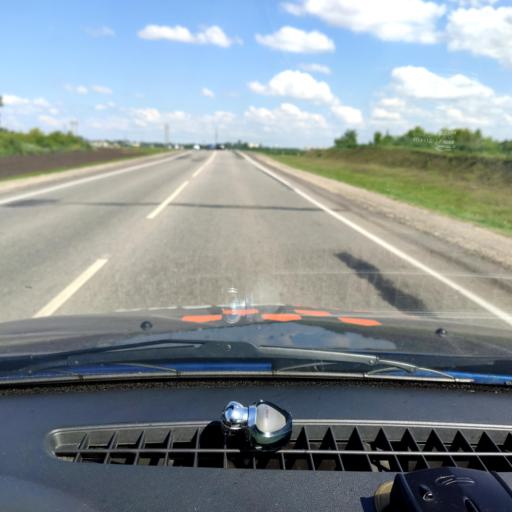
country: RU
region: Orjol
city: Livny
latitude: 52.4409
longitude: 37.5507
